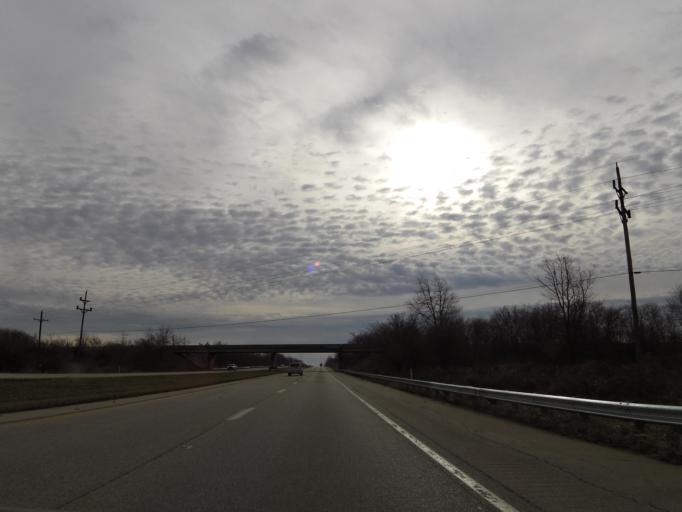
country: US
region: Indiana
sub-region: Boone County
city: Thorntown
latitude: 39.9671
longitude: -86.6542
